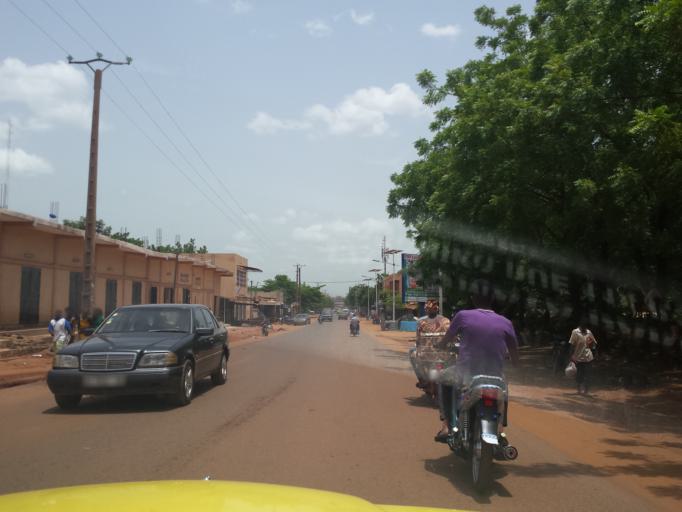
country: ML
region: Bamako
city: Bamako
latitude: 12.6061
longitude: -7.9610
